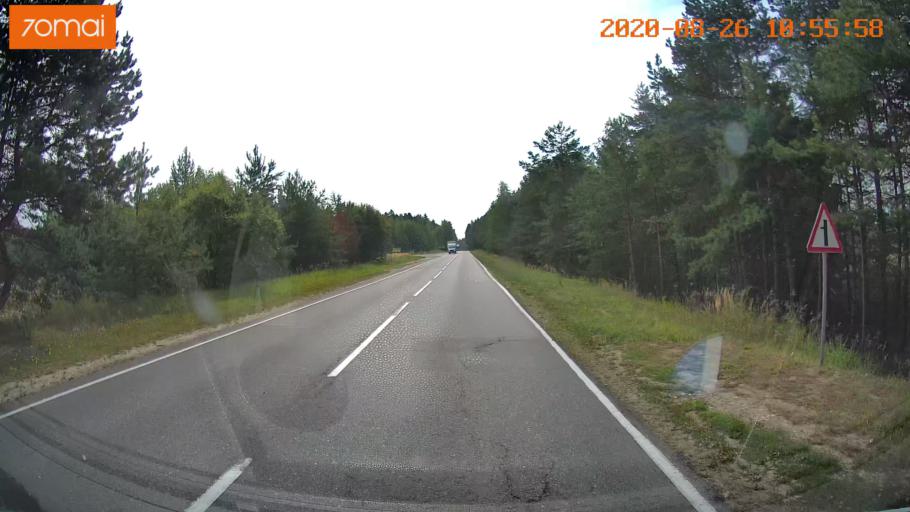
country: RU
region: Rjazan
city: Izhevskoye
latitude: 54.6098
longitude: 41.1827
